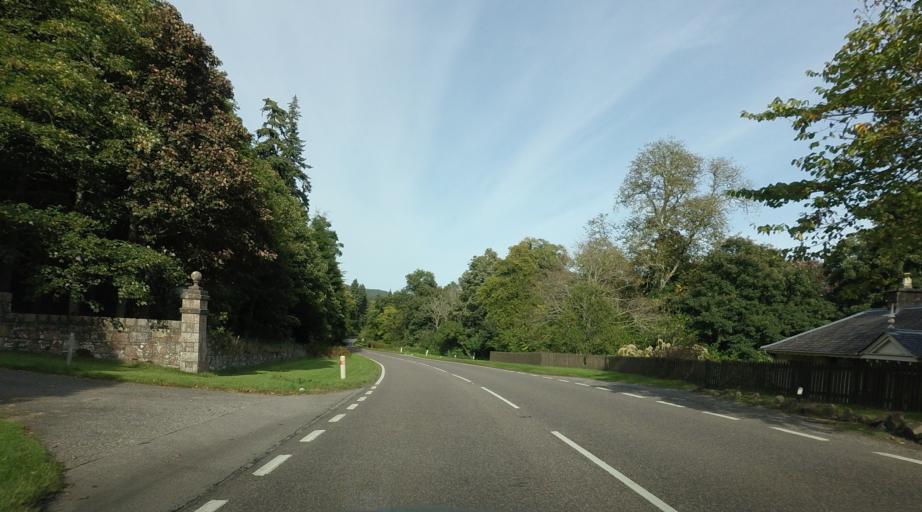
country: GB
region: Scotland
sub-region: Highland
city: Inverness
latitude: 57.4164
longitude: -4.3286
